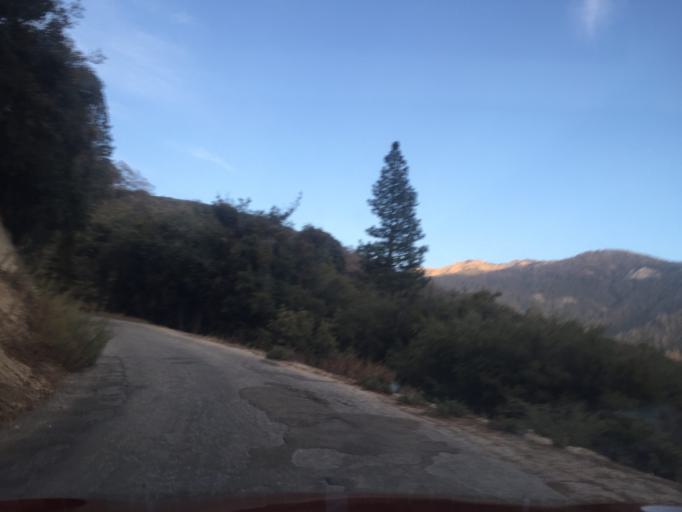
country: US
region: California
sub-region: Tulare County
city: Three Rivers
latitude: 36.4449
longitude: -118.7119
